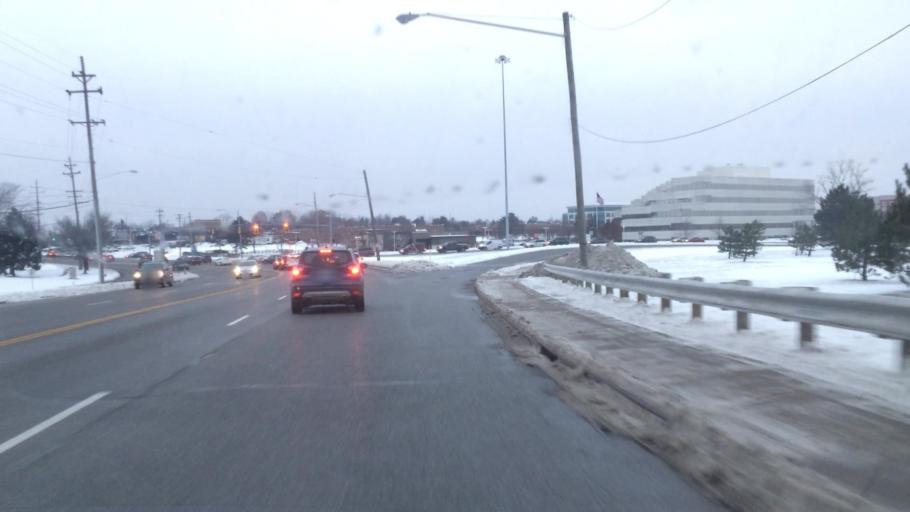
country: US
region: Ohio
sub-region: Cuyahoga County
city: Beachwood
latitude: 41.4639
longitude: -81.4914
